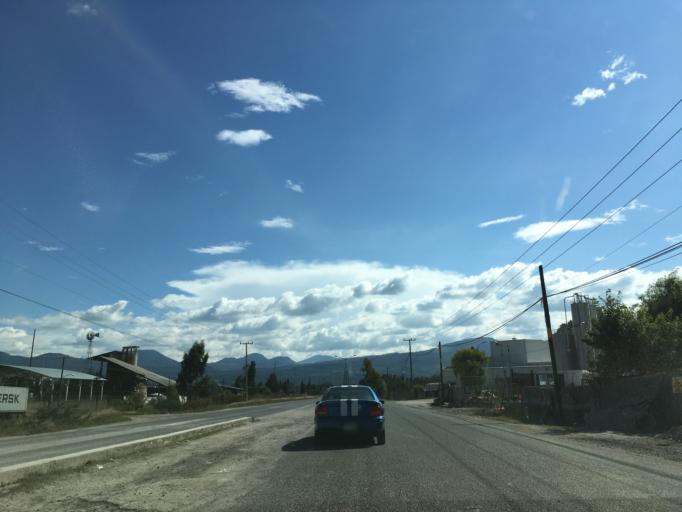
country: MX
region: Michoacan
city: Zacapu
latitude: 19.8318
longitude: -101.7721
